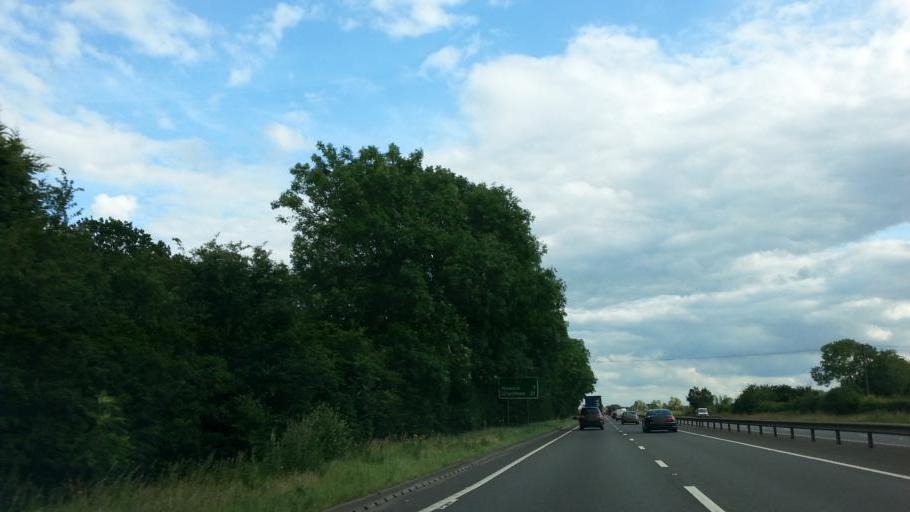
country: GB
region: England
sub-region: Nottinghamshire
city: South Collingham
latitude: 53.1622
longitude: -0.8081
